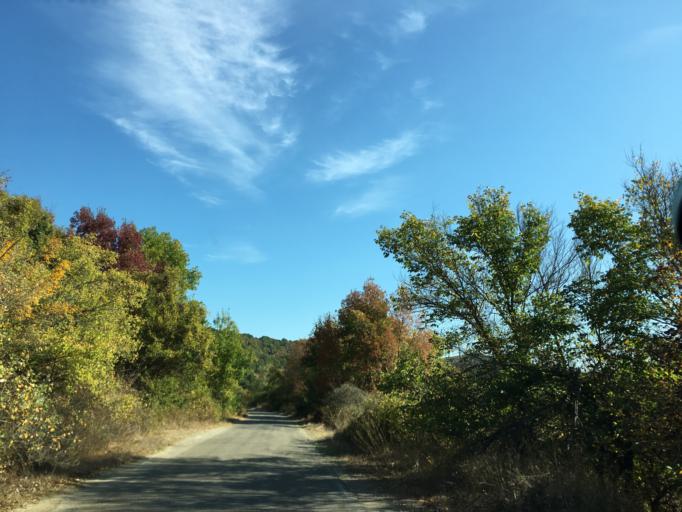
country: BG
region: Khaskovo
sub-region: Obshtina Ivaylovgrad
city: Ivaylovgrad
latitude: 41.4326
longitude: 26.1339
